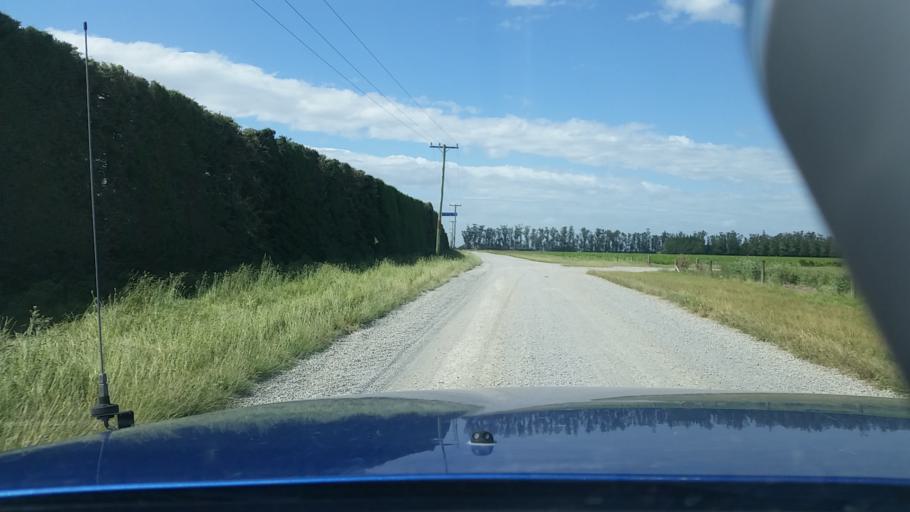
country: NZ
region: Canterbury
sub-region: Ashburton District
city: Ashburton
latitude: -43.9542
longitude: 171.9044
